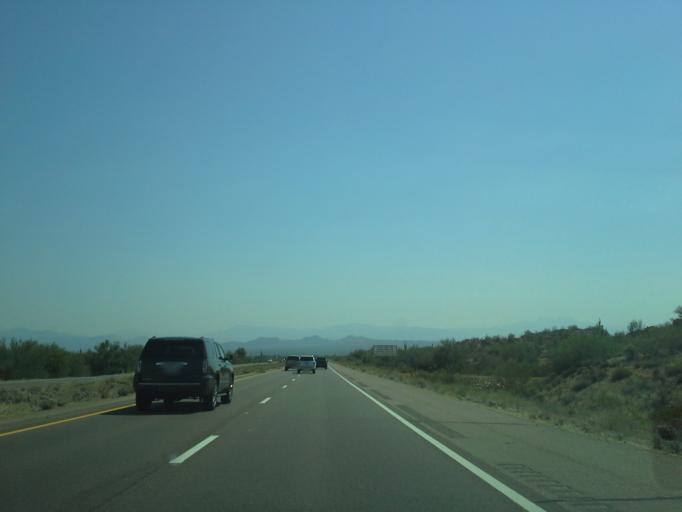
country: US
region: Arizona
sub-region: Maricopa County
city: Fountain Hills
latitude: 33.5690
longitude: -111.7024
